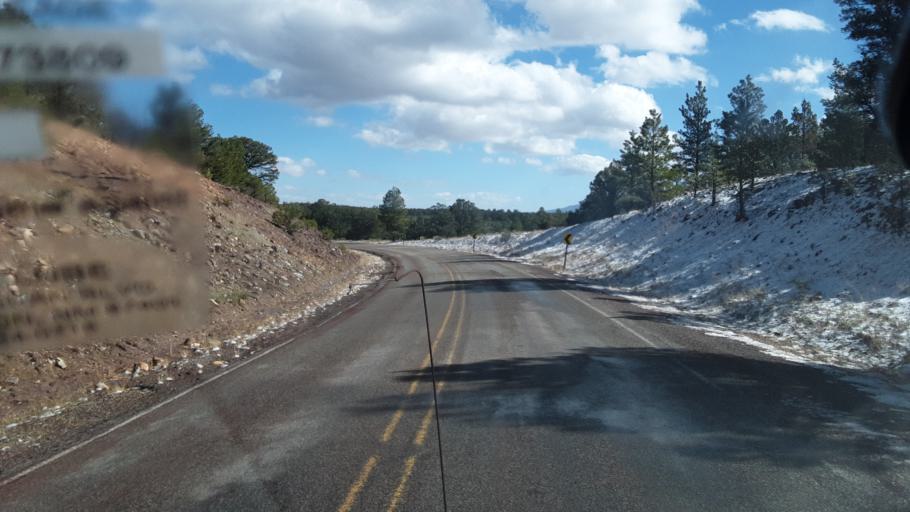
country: US
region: New Mexico
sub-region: Rio Arriba County
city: Santa Teresa
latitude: 36.1946
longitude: -106.7424
